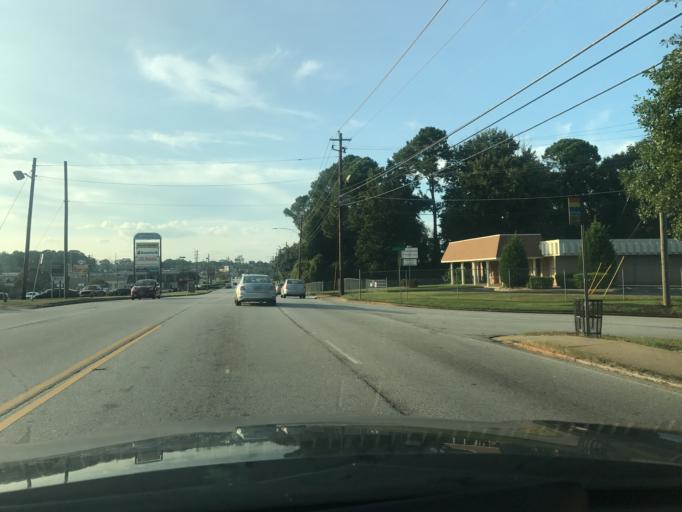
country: US
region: Georgia
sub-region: DeKalb County
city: Belvedere Park
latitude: 33.7509
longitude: -84.2647
